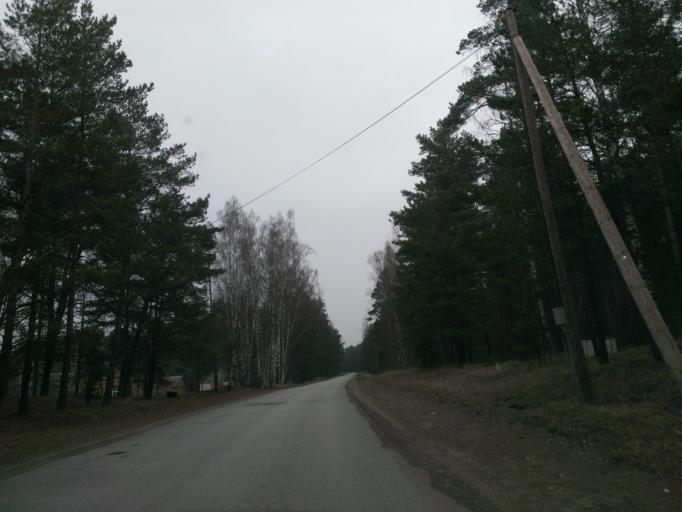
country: LV
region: Salacgrivas
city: Ainazi
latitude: 58.0232
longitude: 24.4549
